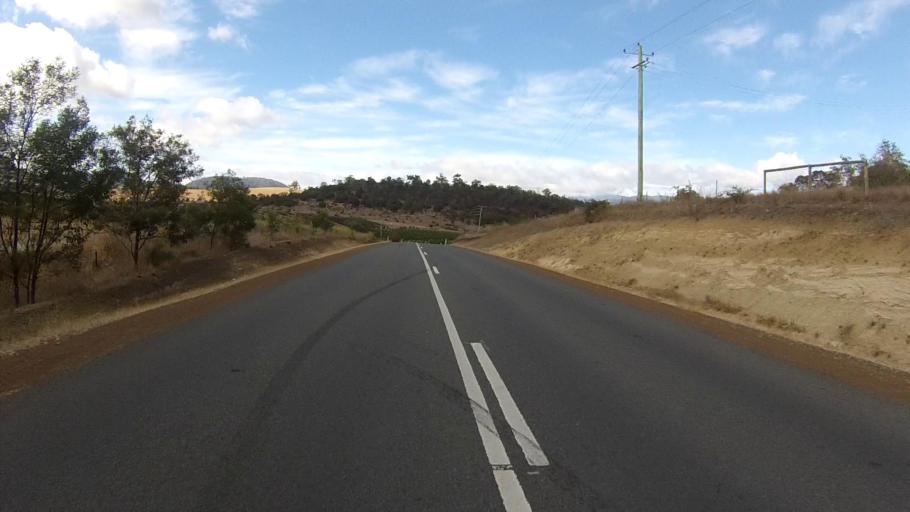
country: AU
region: Tasmania
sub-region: Brighton
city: Old Beach
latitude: -42.7392
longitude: 147.2881
